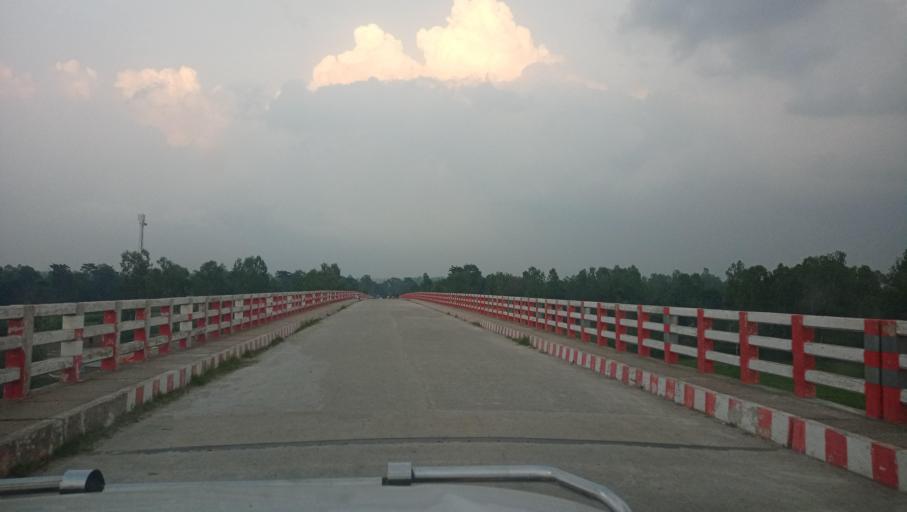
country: BD
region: Dhaka
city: Sherpur
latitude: 25.1768
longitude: 89.7924
